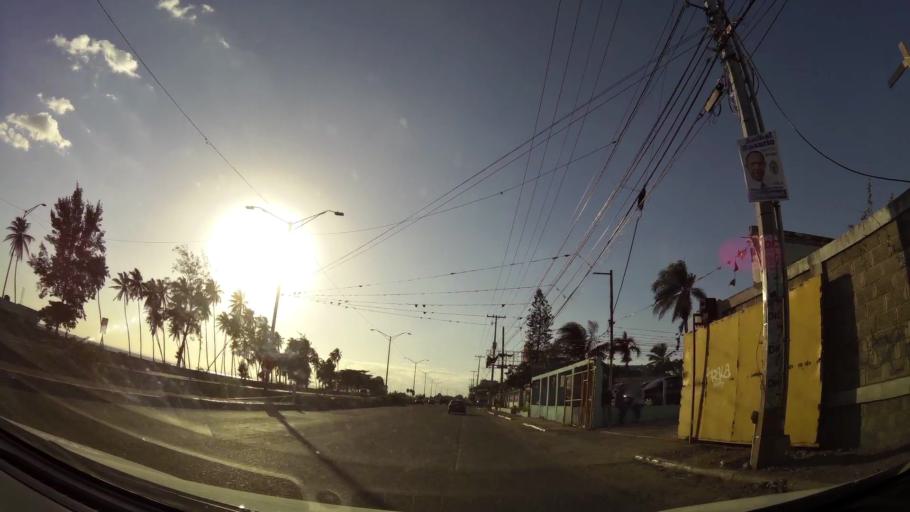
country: DO
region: Santo Domingo
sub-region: Santo Domingo
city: Santo Domingo Este
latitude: 18.4662
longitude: -69.8220
